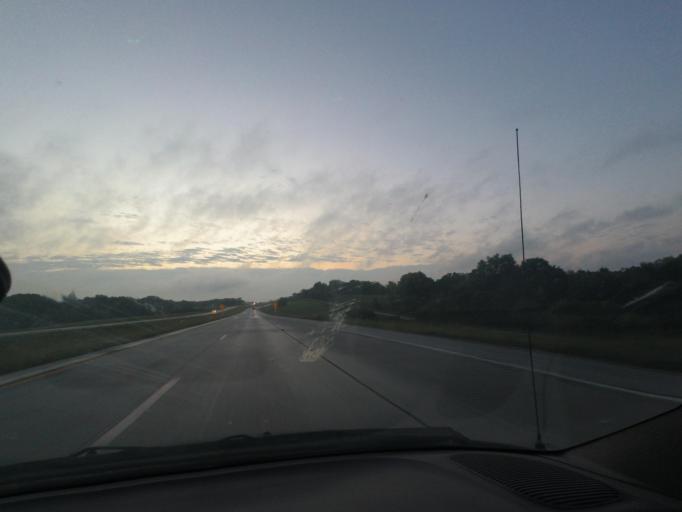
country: US
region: Missouri
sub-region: Linn County
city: Marceline
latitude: 39.7610
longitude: -92.9352
